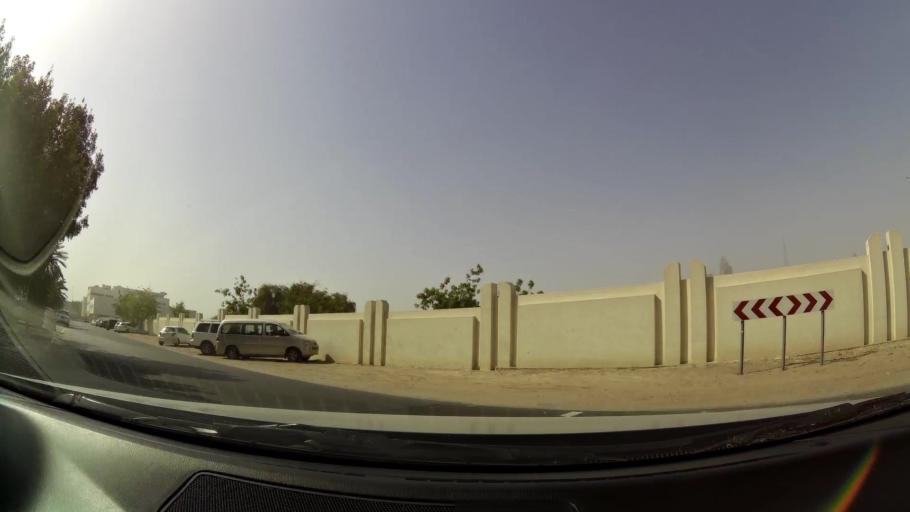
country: AE
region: Dubai
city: Dubai
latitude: 25.1704
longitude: 55.2462
